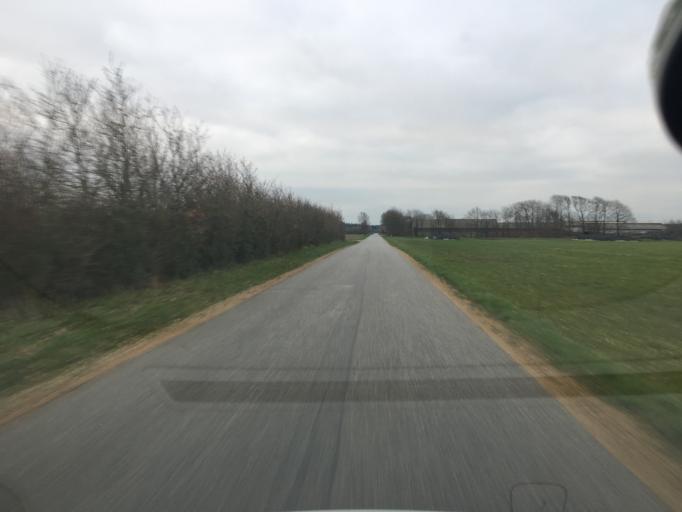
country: DK
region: South Denmark
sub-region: Tonder Kommune
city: Logumkloster
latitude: 55.0322
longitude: 9.0308
